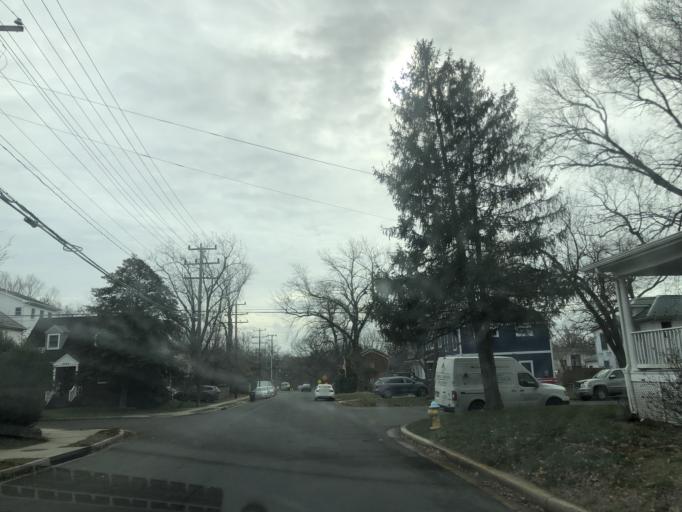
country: US
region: Virginia
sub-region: Fairfax County
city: Baileys Crossroads
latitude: 38.8728
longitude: -77.1294
